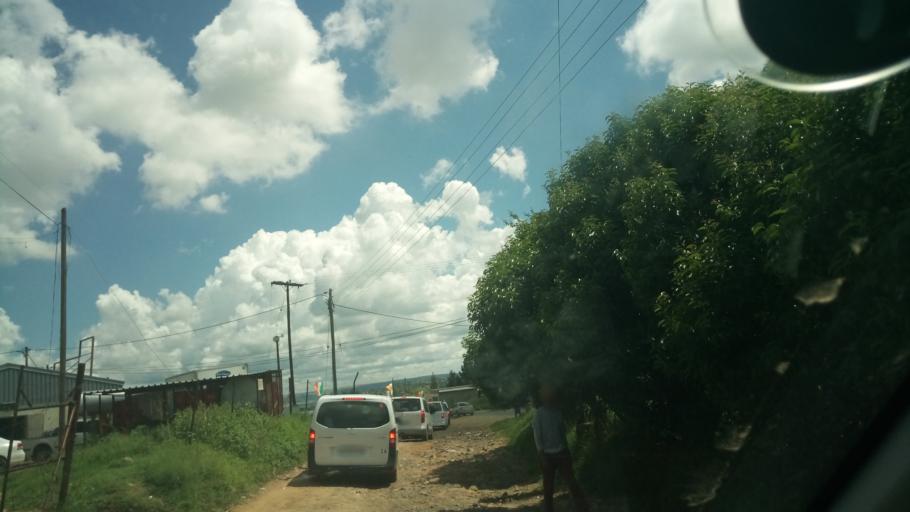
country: LS
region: Maseru
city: Maseru
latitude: -29.3507
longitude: 27.5359
